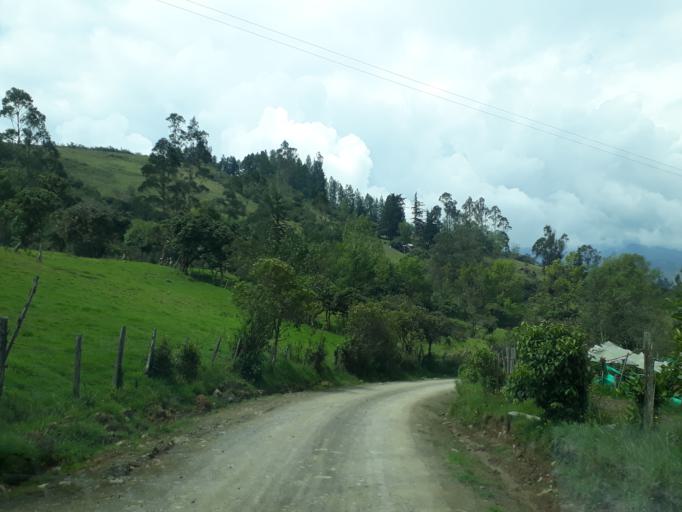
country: CO
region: Cundinamarca
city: Macheta
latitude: 5.0962
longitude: -73.5542
